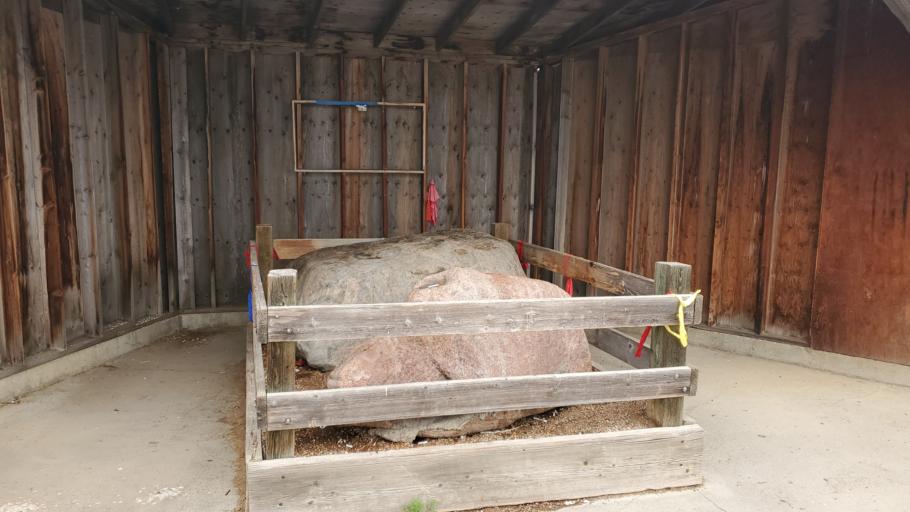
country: US
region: Montana
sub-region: Phillips County
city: Malta
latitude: 48.4697
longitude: -107.5494
